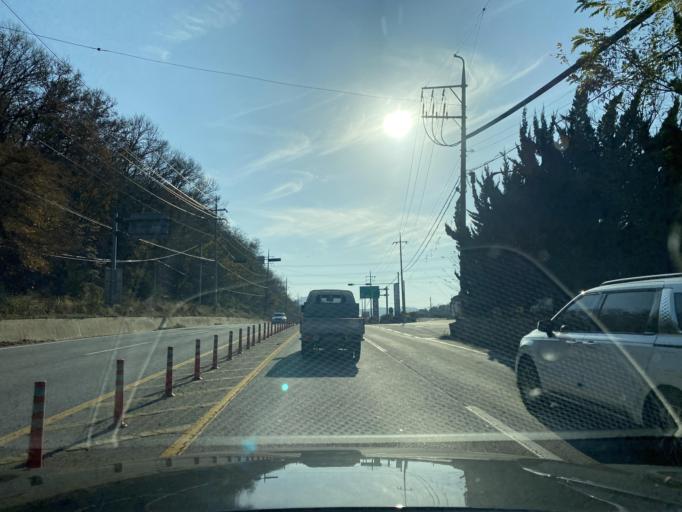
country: KR
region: Chungcheongnam-do
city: Asan
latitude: 36.7685
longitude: 126.9264
